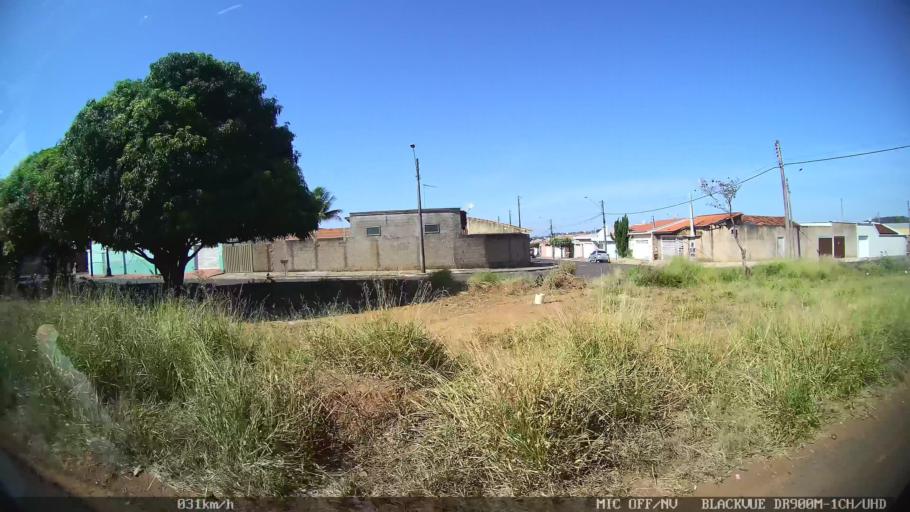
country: BR
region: Sao Paulo
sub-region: Batatais
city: Batatais
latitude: -20.8773
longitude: -47.5962
